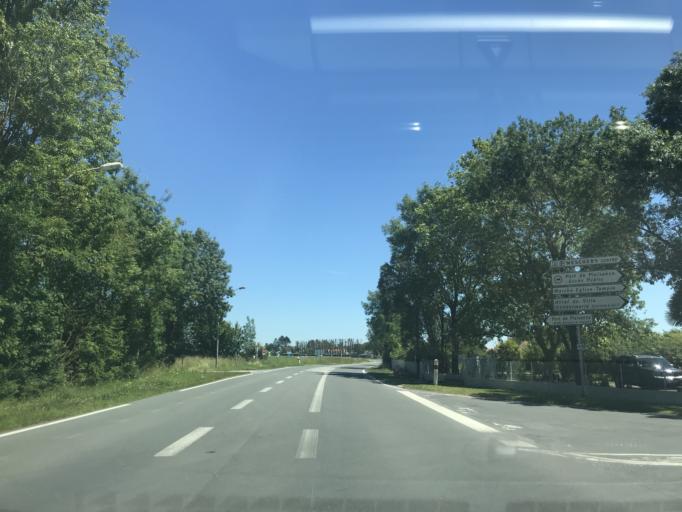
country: FR
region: Poitou-Charentes
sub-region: Departement de la Charente-Maritime
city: Meschers-sur-Gironde
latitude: 45.5629
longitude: -0.9460
